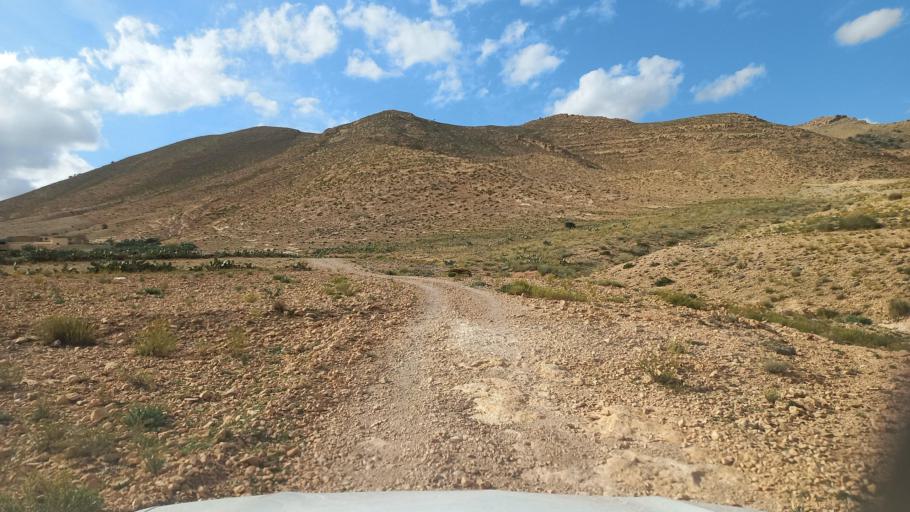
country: TN
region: Al Qasrayn
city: Sbiba
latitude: 35.4572
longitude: 9.0694
